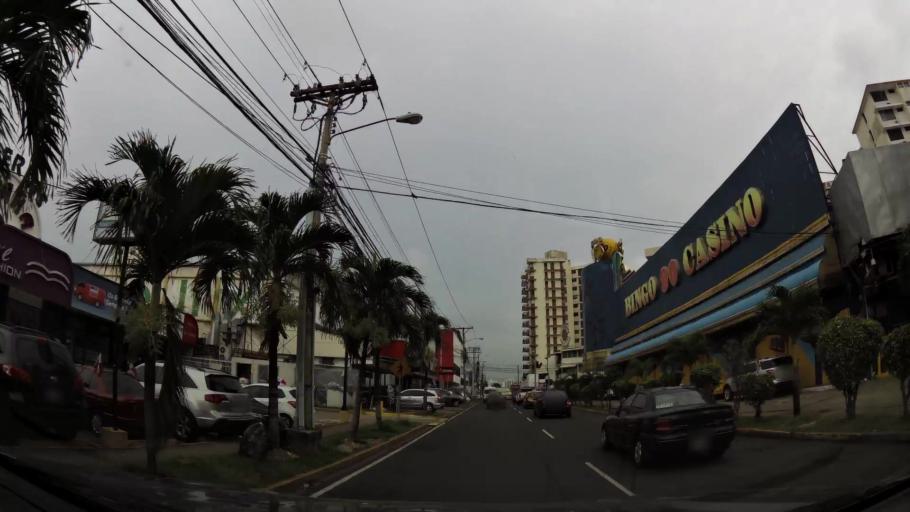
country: PA
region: Panama
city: Panama
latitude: 8.9889
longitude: -79.5216
